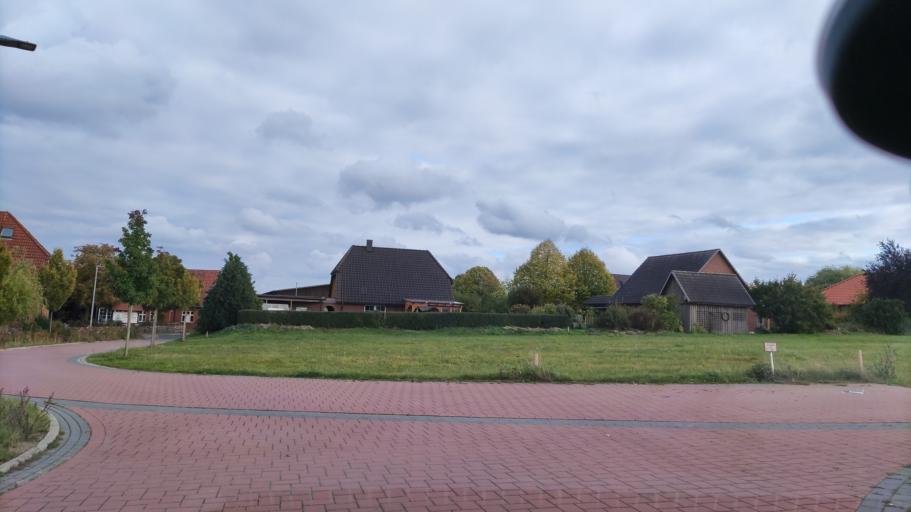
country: DE
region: Lower Saxony
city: Romstedt
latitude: 53.0936
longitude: 10.6481
